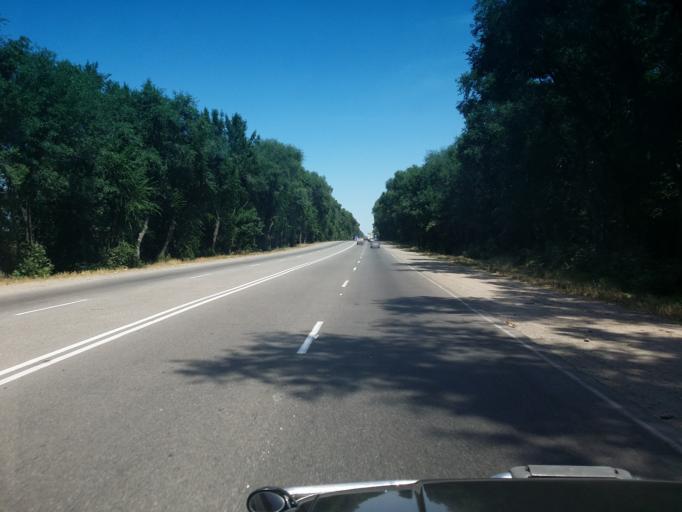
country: KZ
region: Almaty Oblysy
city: Talghar
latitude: 43.4085
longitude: 77.3127
